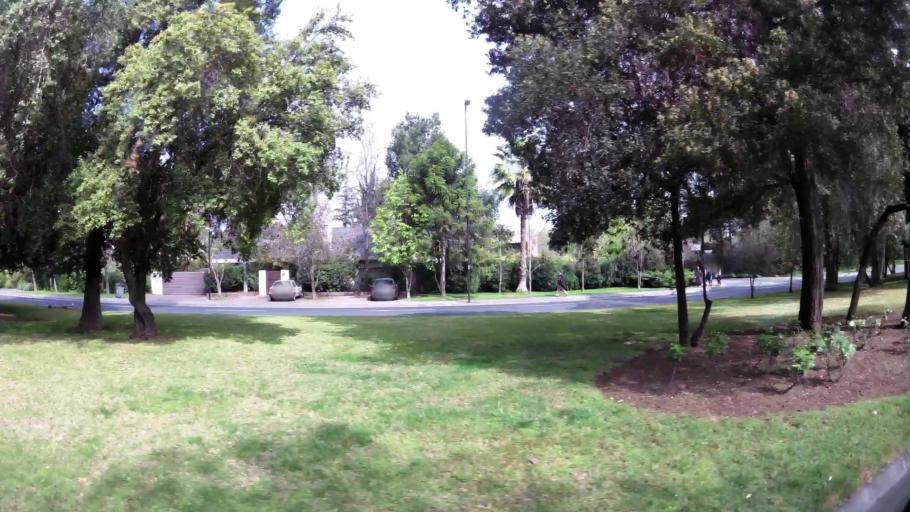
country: CL
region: Santiago Metropolitan
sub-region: Provincia de Santiago
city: Villa Presidente Frei, Nunoa, Santiago, Chile
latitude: -33.3753
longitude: -70.5704
